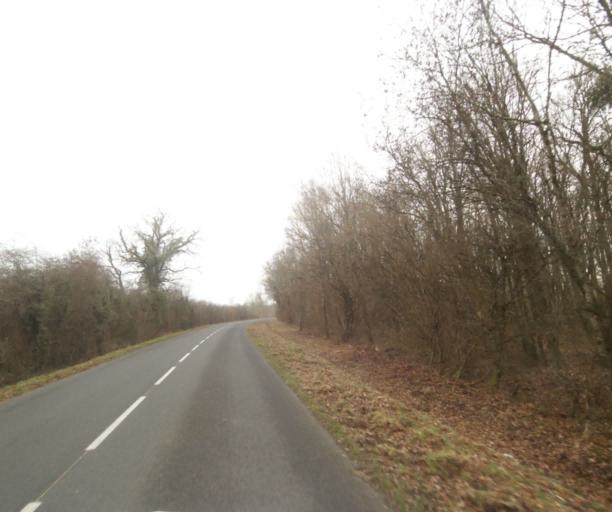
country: FR
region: Champagne-Ardenne
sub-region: Departement de la Marne
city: Pargny-sur-Saulx
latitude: 48.7377
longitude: 4.8792
